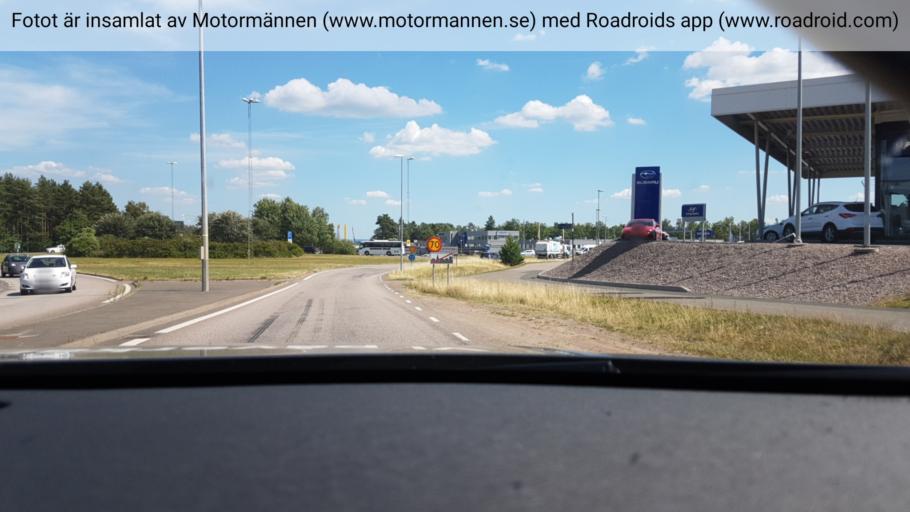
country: SE
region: Vaestra Goetaland
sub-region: Skovde Kommun
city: Skoevde
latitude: 58.4197
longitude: 13.8661
